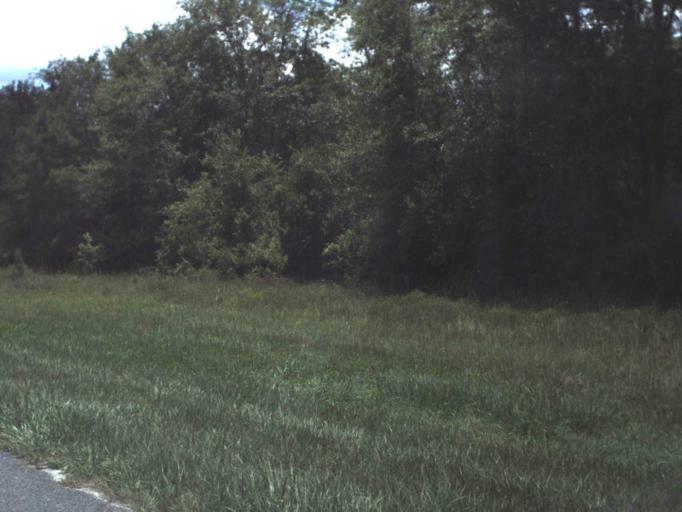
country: US
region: Georgia
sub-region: Echols County
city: Statenville
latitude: 30.5999
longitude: -83.0136
